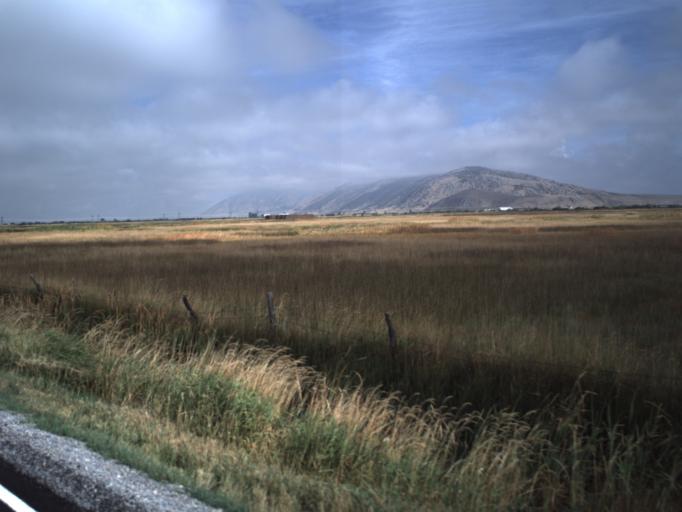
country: US
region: Utah
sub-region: Rich County
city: Randolph
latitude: 41.5071
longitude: -111.1274
